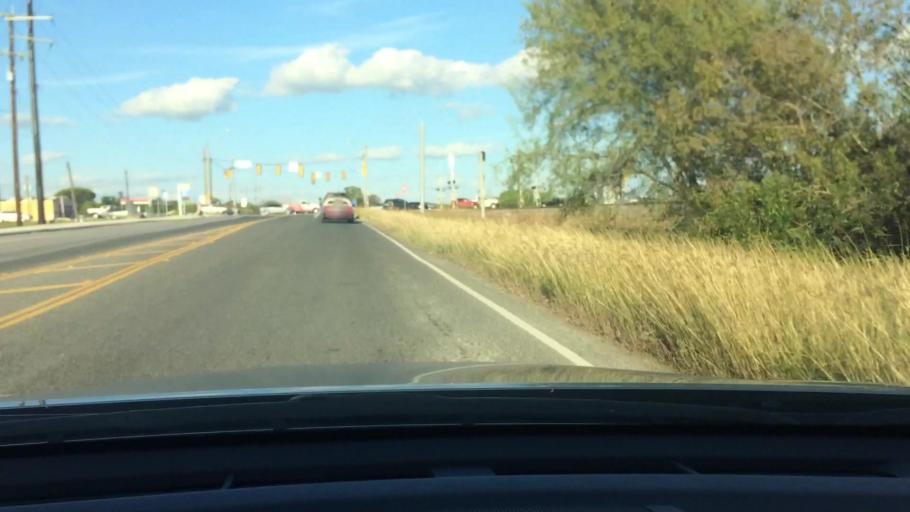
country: US
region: Texas
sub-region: Bexar County
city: Windcrest
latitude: 29.4966
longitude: -98.3503
